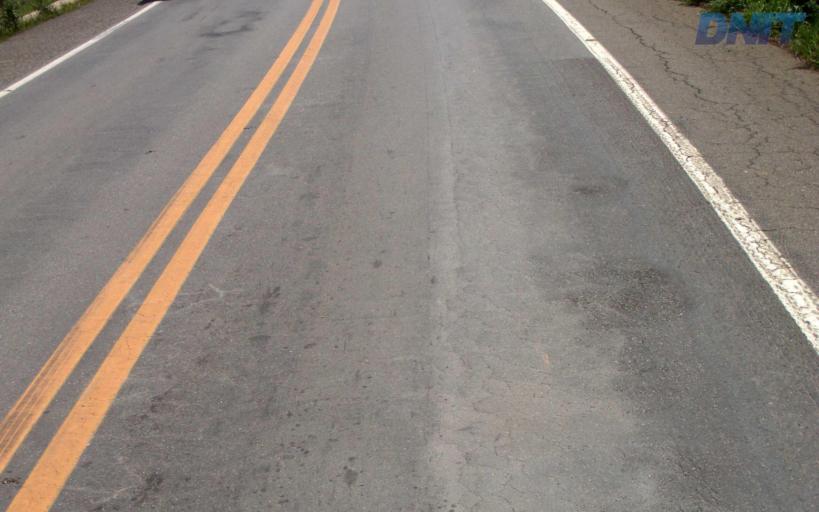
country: BR
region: Minas Gerais
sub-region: Governador Valadares
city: Governador Valadares
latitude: -19.0212
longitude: -42.1433
